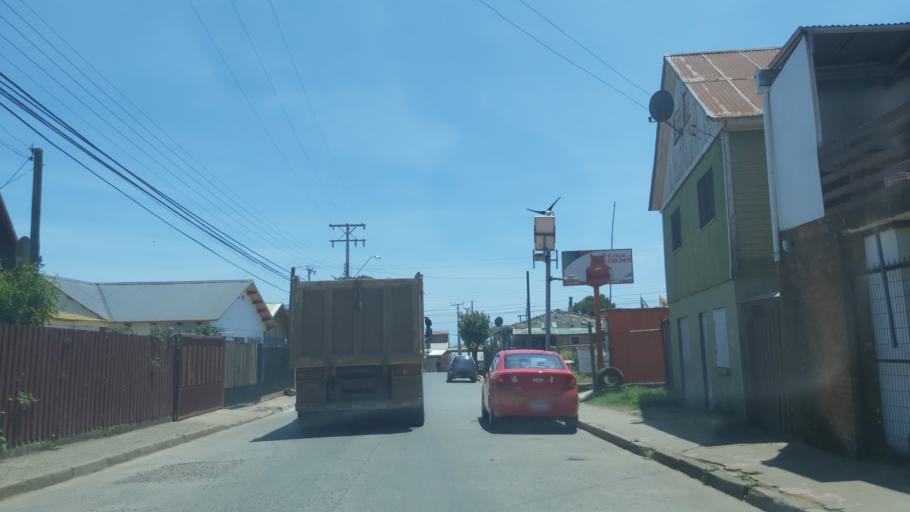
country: CL
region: Maule
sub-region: Provincia de Cauquenes
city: Cauquenes
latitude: -35.8143
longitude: -72.5733
